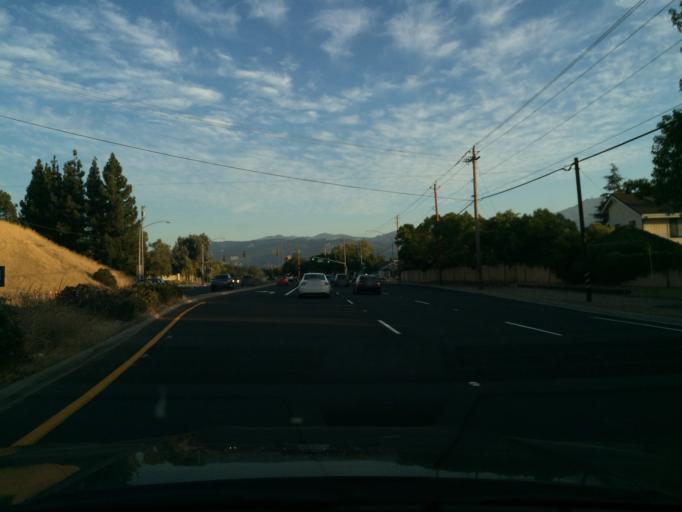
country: US
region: California
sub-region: Santa Clara County
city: Seven Trees
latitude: 37.2377
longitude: -121.8736
